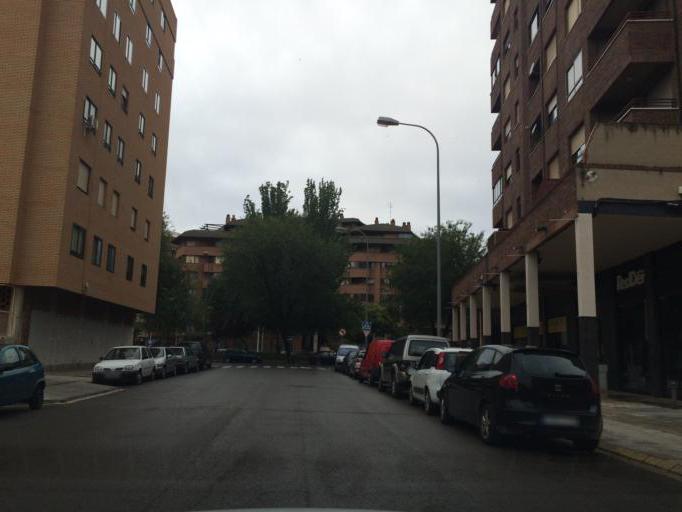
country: ES
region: Castille-La Mancha
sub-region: Provincia de Albacete
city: Albacete
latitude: 39.0006
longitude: -1.8538
